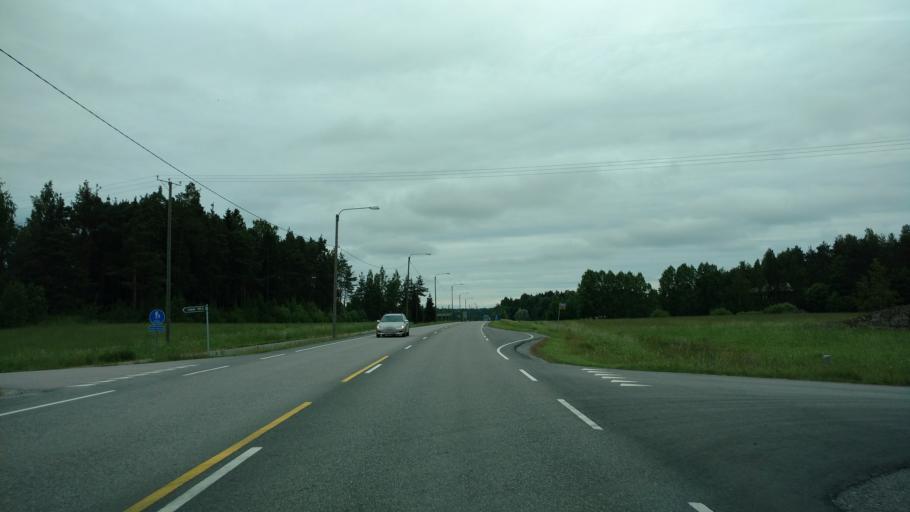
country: FI
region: Varsinais-Suomi
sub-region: Salo
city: Halikko
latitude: 60.4172
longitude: 23.0510
